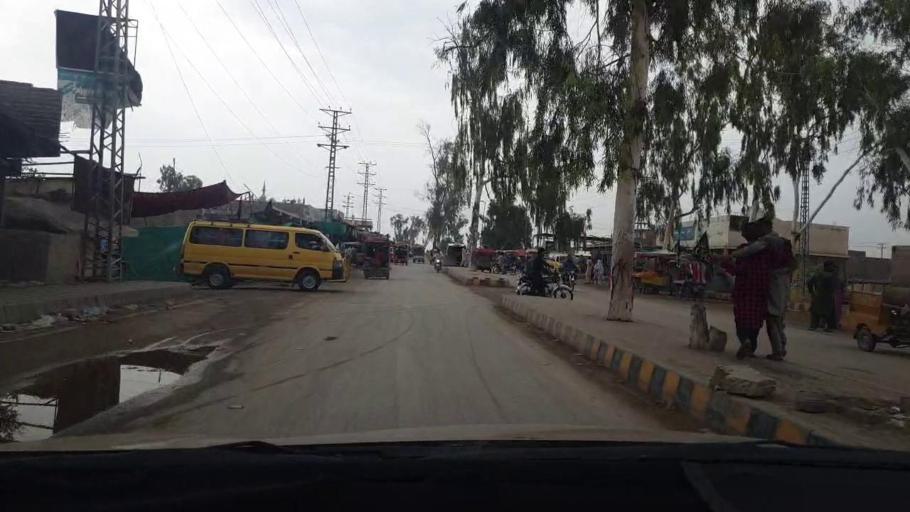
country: PK
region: Sindh
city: Larkana
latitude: 27.5801
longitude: 68.2218
